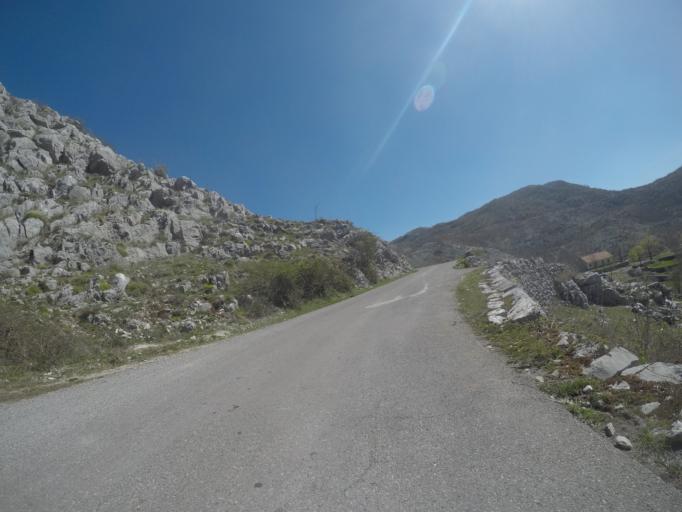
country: ME
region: Cetinje
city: Cetinje
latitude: 42.4960
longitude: 18.8754
